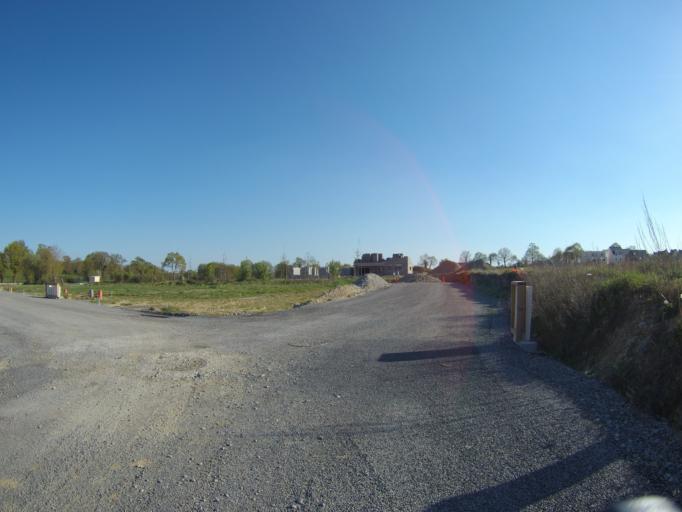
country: FR
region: Brittany
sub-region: Departement d'Ille-et-Vilaine
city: Vern-sur-Seiche
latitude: 48.0402
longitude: -1.5920
